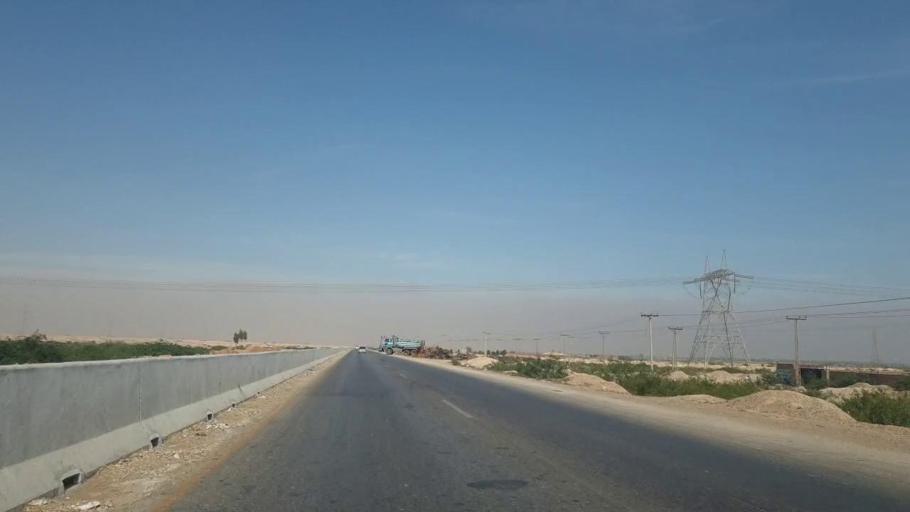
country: PK
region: Sindh
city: Jamshoro
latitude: 25.4835
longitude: 68.2720
